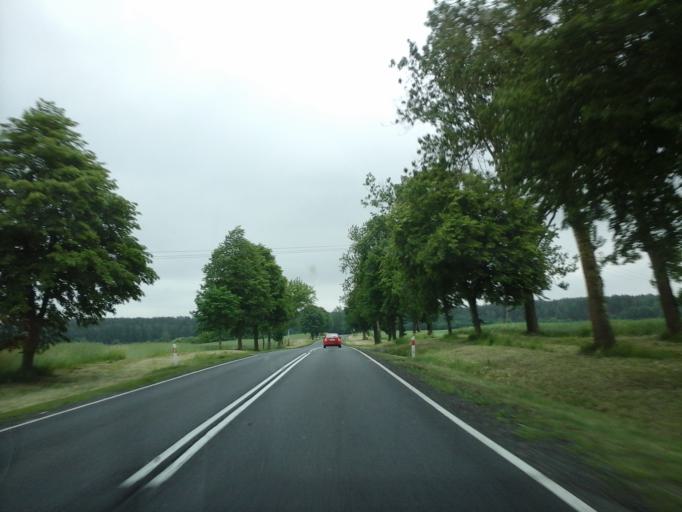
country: PL
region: West Pomeranian Voivodeship
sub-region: Powiat drawski
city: Kalisz Pomorski
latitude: 53.2928
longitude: 15.9355
